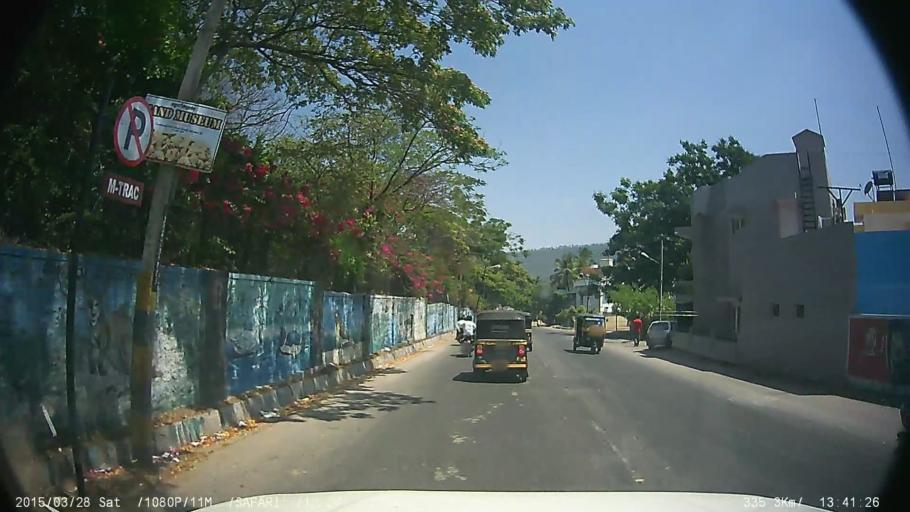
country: IN
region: Karnataka
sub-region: Mysore
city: Mysore
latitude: 12.3013
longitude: 76.6644
